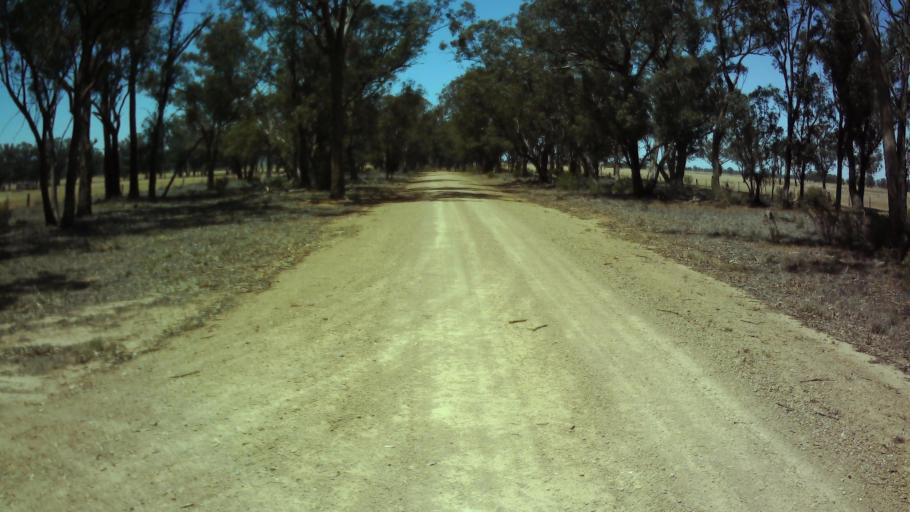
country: AU
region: New South Wales
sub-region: Weddin
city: Grenfell
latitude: -34.0421
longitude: 148.0125
